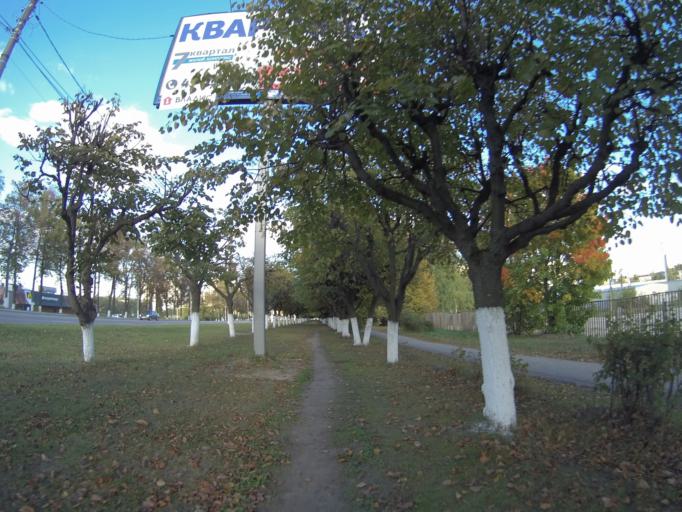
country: RU
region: Vladimir
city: Vladimir
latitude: 56.1147
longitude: 40.3386
